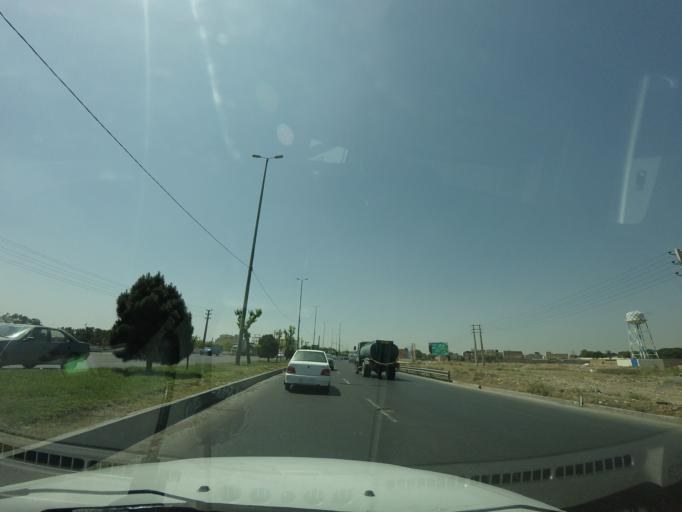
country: IR
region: Tehran
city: Eslamshahr
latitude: 35.5906
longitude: 51.2905
